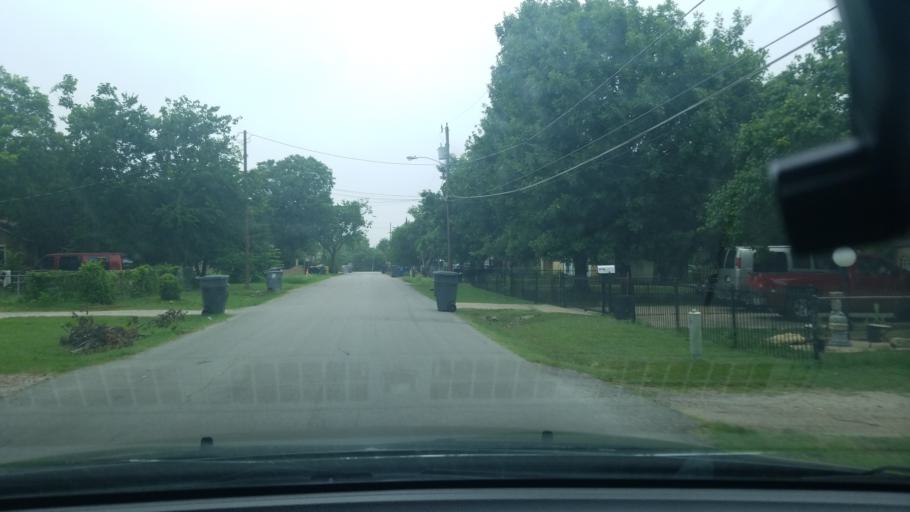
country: US
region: Texas
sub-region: Dallas County
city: Balch Springs
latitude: 32.7616
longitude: -96.6766
